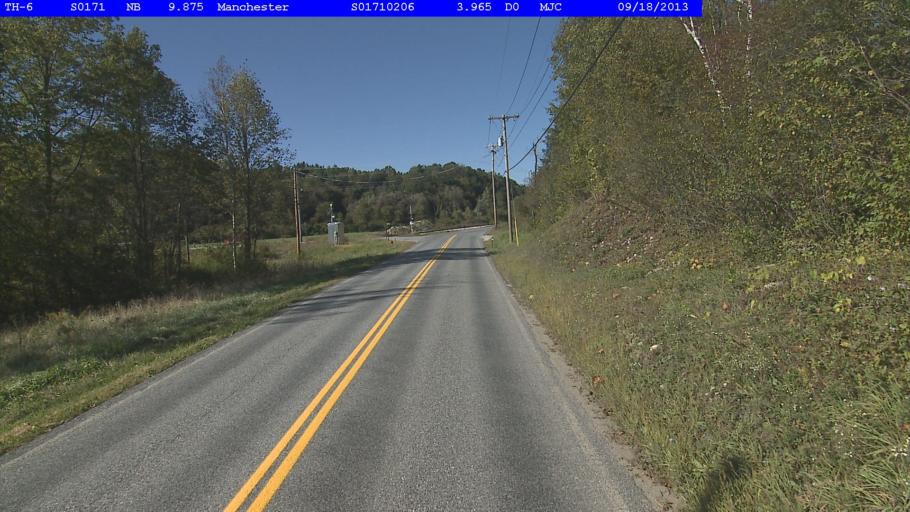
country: US
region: Vermont
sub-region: Bennington County
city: Manchester Center
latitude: 43.1613
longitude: -73.0539
